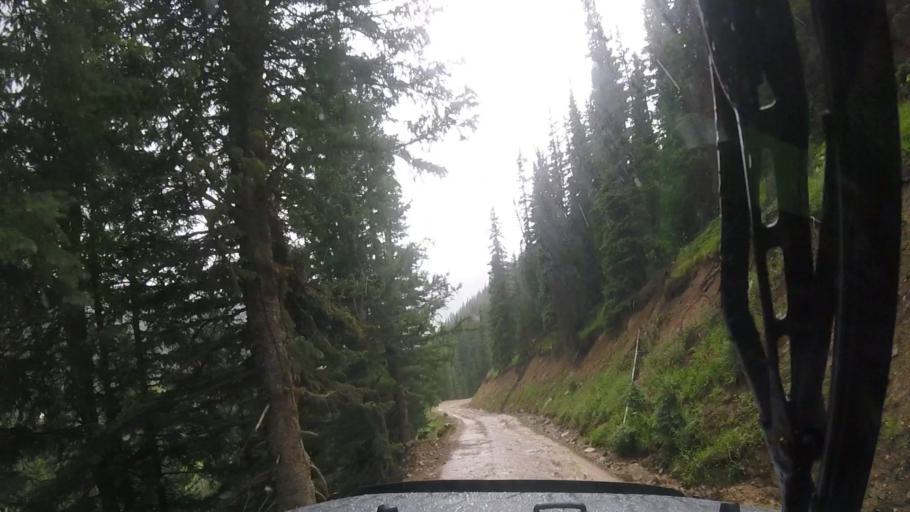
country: US
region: Colorado
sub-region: San Juan County
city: Silverton
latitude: 37.9037
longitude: -107.6471
